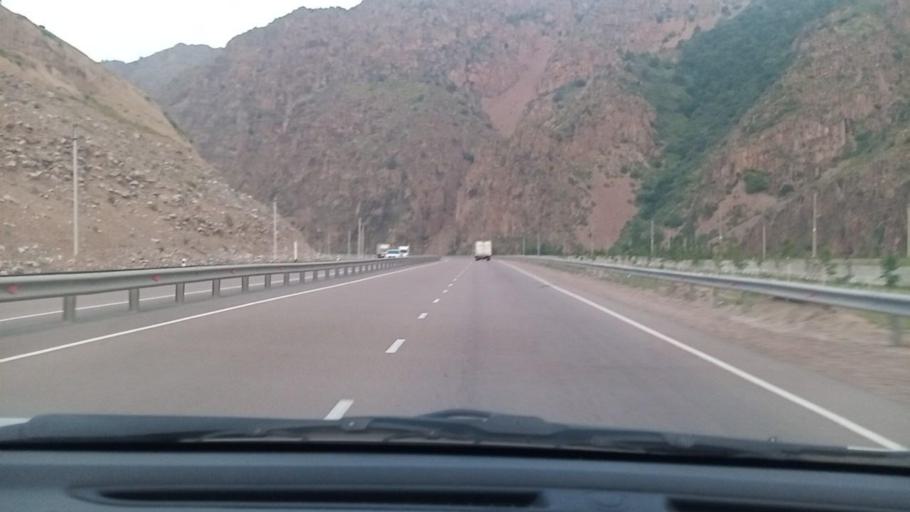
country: UZ
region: Toshkent
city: Angren
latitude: 41.1259
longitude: 70.3625
